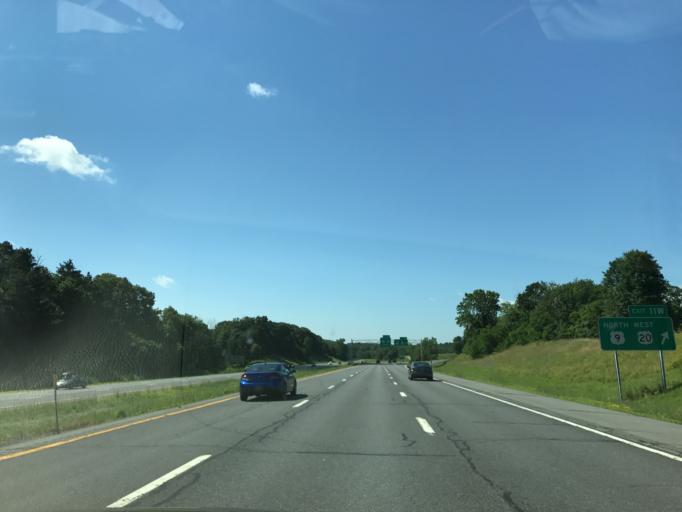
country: US
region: New York
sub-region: Rensselaer County
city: East Greenbush
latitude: 42.5655
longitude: -73.6789
